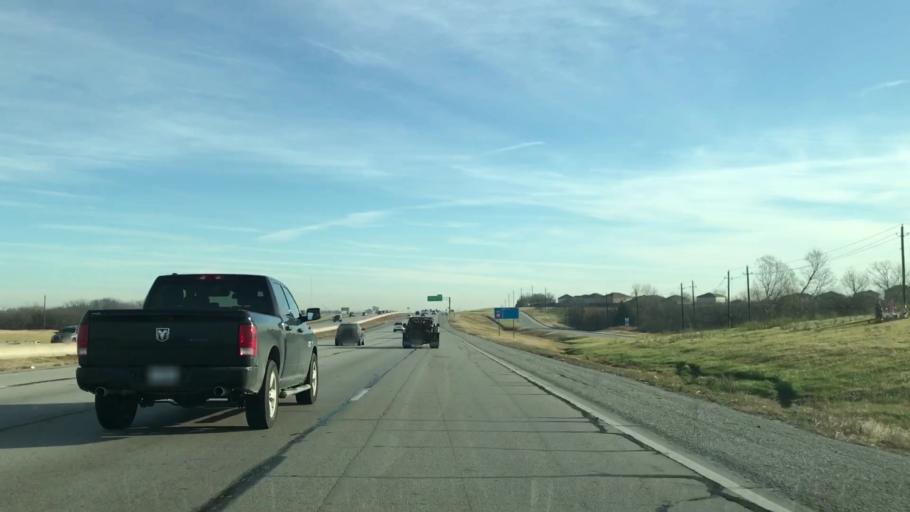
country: US
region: Texas
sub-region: Tarrant County
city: Sansom Park
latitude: 32.8170
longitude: -97.4038
